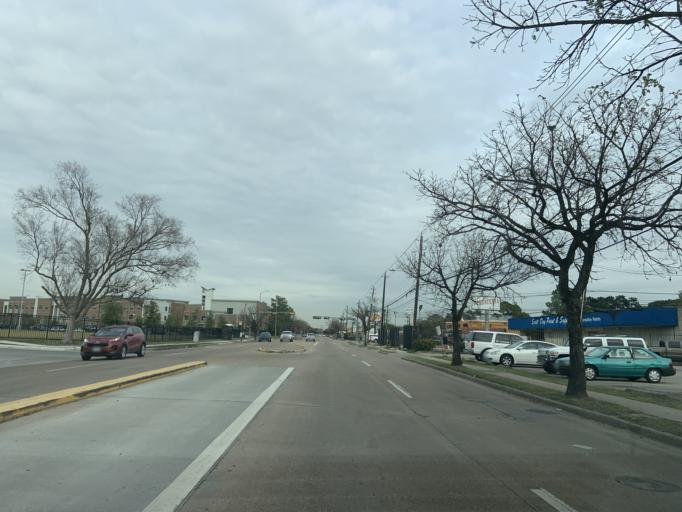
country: US
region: Texas
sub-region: Harris County
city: Bellaire
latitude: 29.6838
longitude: -95.5145
